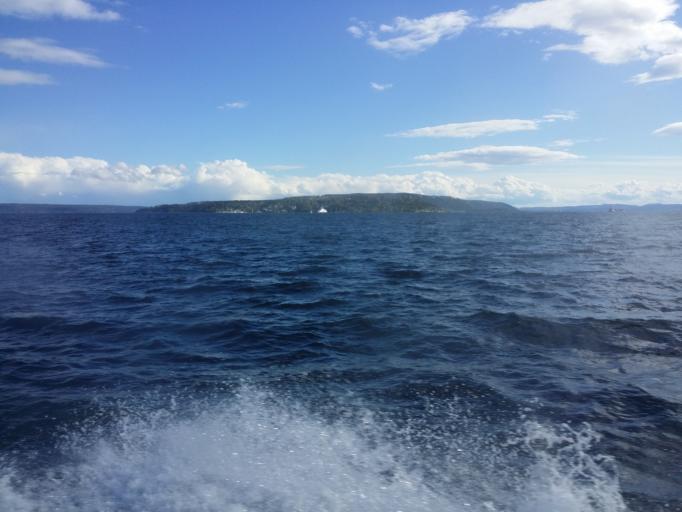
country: NO
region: Akershus
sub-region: Nesodden
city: Nesoddtangen
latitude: 59.8925
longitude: 10.6642
